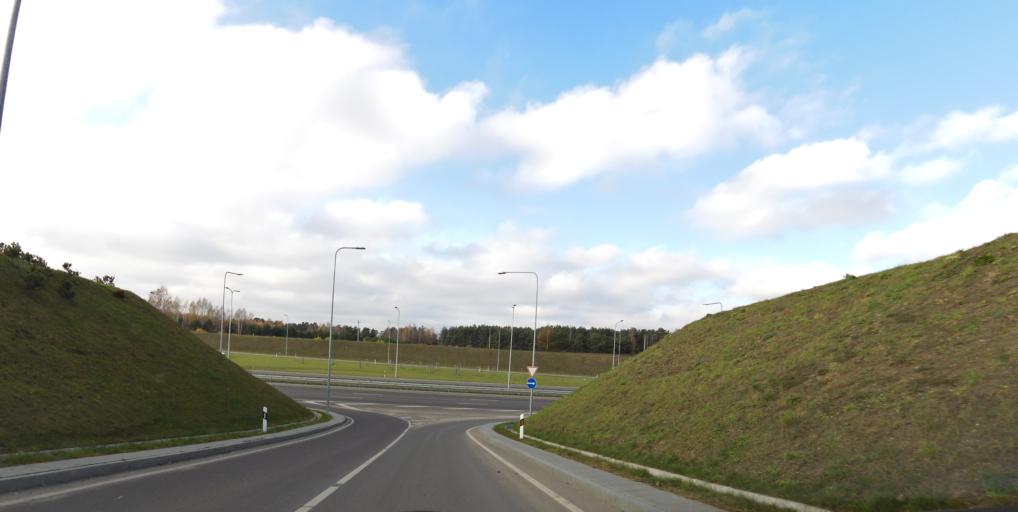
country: LT
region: Vilnius County
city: Lazdynai
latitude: 54.6844
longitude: 25.1967
